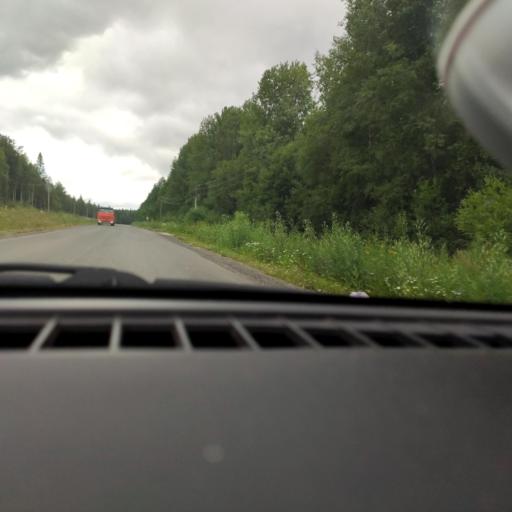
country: RU
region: Perm
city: Polazna
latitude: 58.3255
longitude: 56.1499
